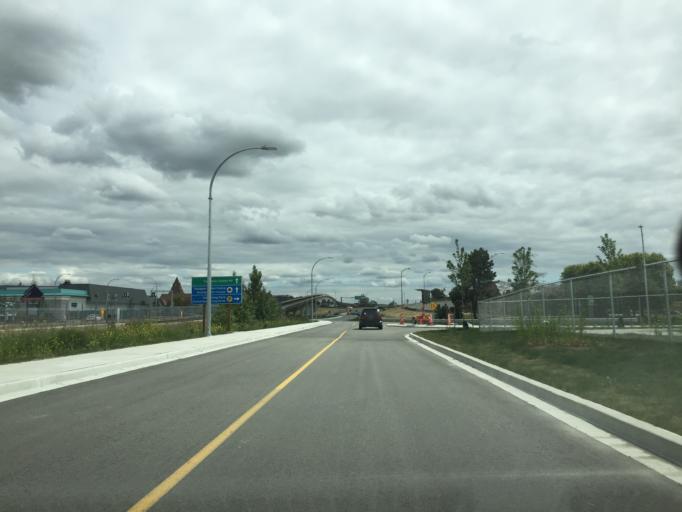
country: CA
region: British Columbia
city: Richmond
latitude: 49.1965
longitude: -123.1442
